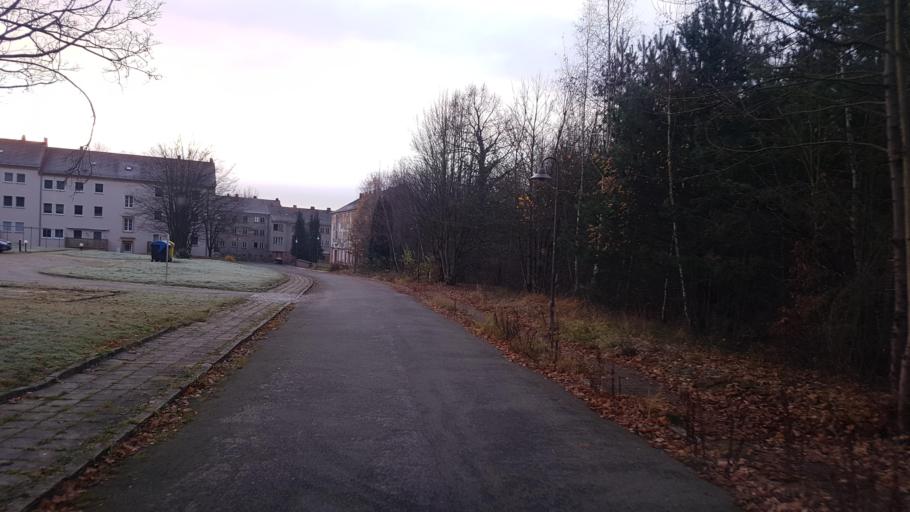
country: DE
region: Brandenburg
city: Lauchhammer
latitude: 51.5017
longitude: 13.7468
